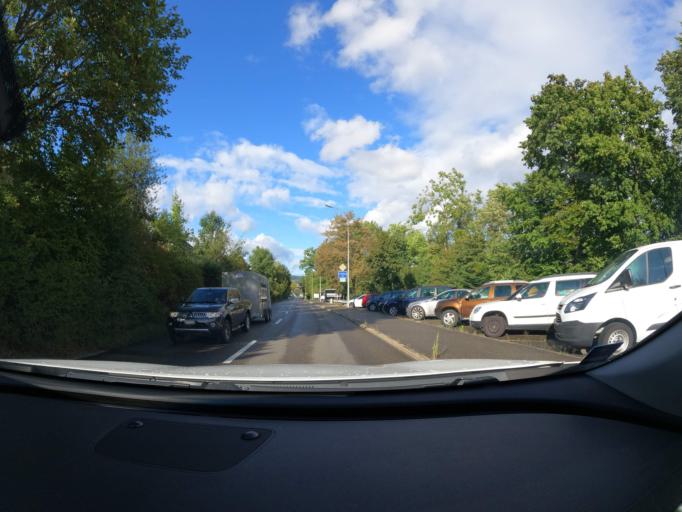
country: CH
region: Aargau
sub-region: Bezirk Lenzburg
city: Lenzburg
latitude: 47.3812
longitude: 8.1737
